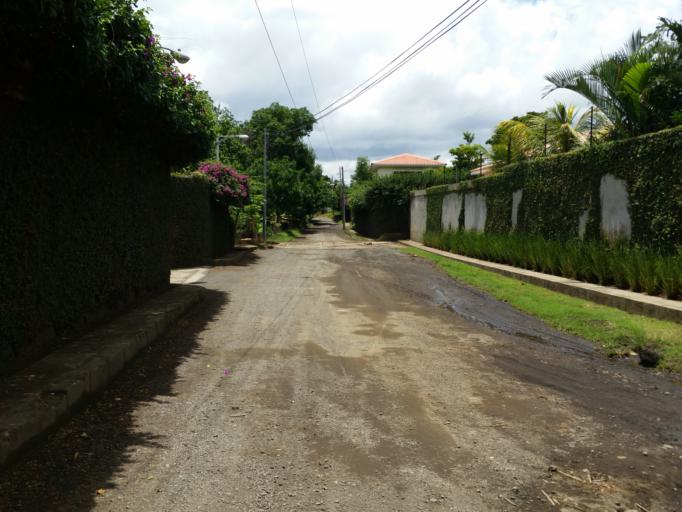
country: NI
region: Managua
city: Managua
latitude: 12.0768
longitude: -86.2530
